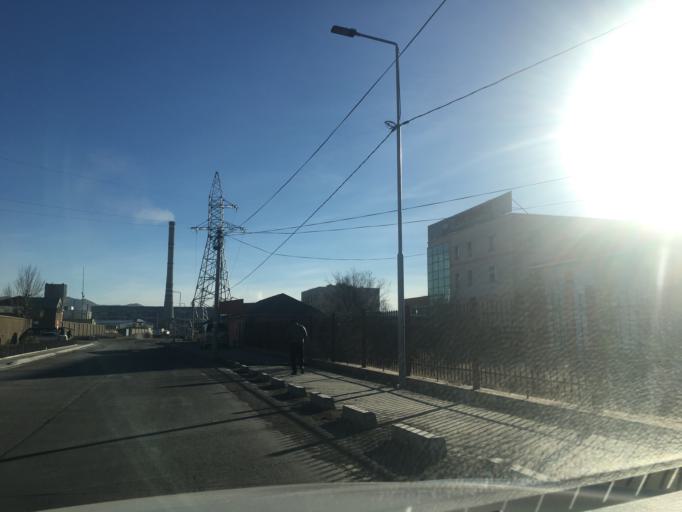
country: MN
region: Ulaanbaatar
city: Ulaanbaatar
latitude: 47.9069
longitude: 106.8027
